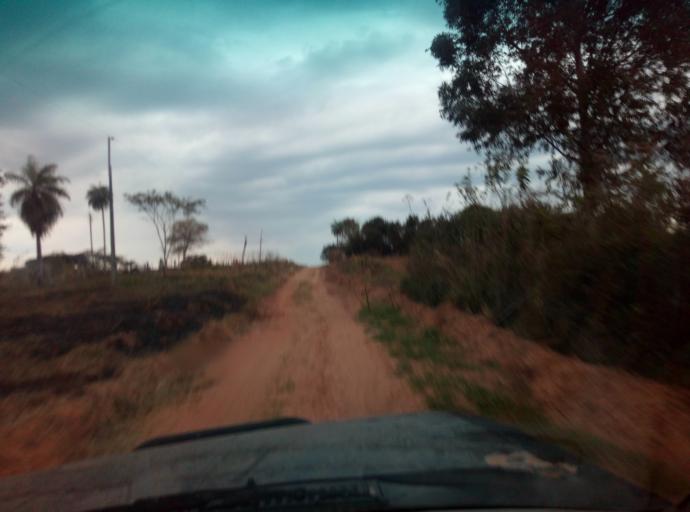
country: PY
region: Caaguazu
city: Doctor Cecilio Baez
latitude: -25.1421
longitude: -56.2241
